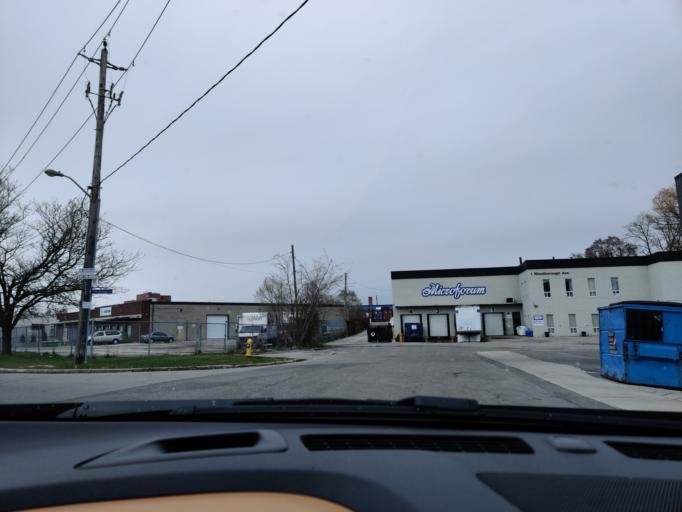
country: CA
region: Ontario
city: Toronto
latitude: 43.6951
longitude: -79.4665
